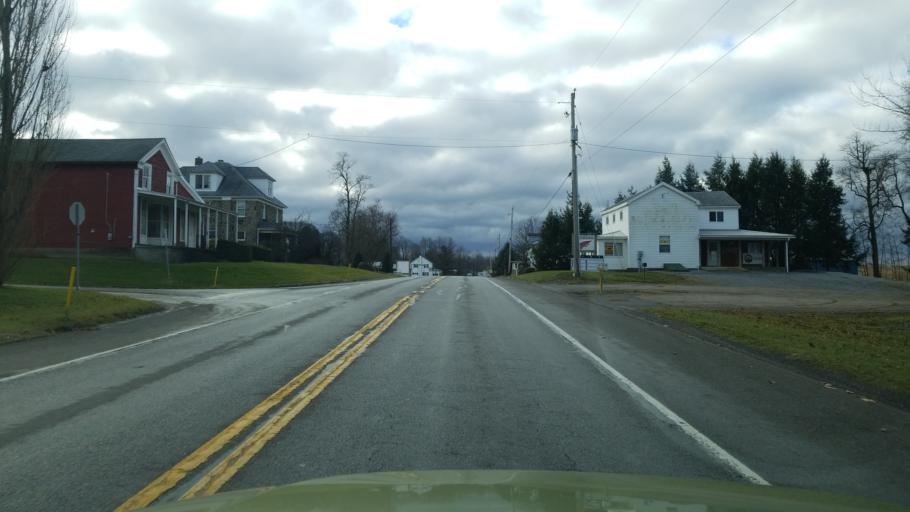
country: US
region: Pennsylvania
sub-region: Jefferson County
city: Punxsutawney
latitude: 40.8577
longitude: -79.0228
